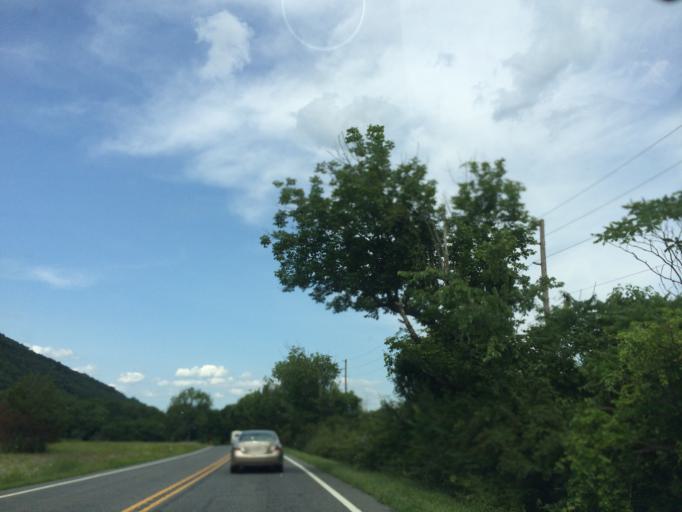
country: US
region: Pennsylvania
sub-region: Pike County
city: Pocono Ranch Lands
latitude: 41.1224
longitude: -74.9573
